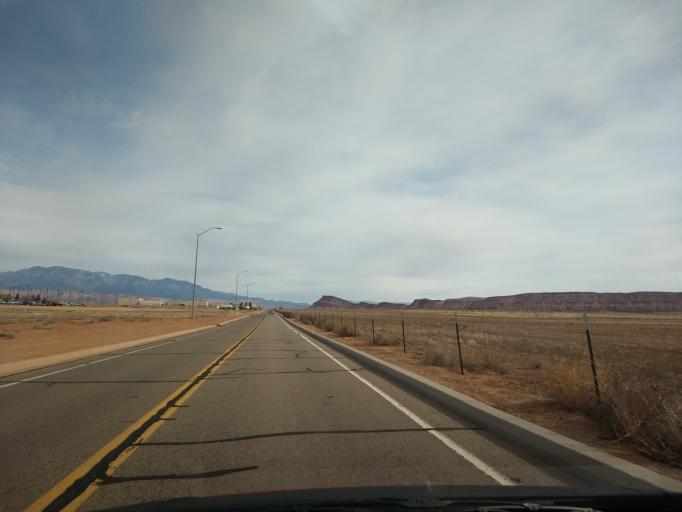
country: US
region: Utah
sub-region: Washington County
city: Washington
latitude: 37.0271
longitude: -113.5071
